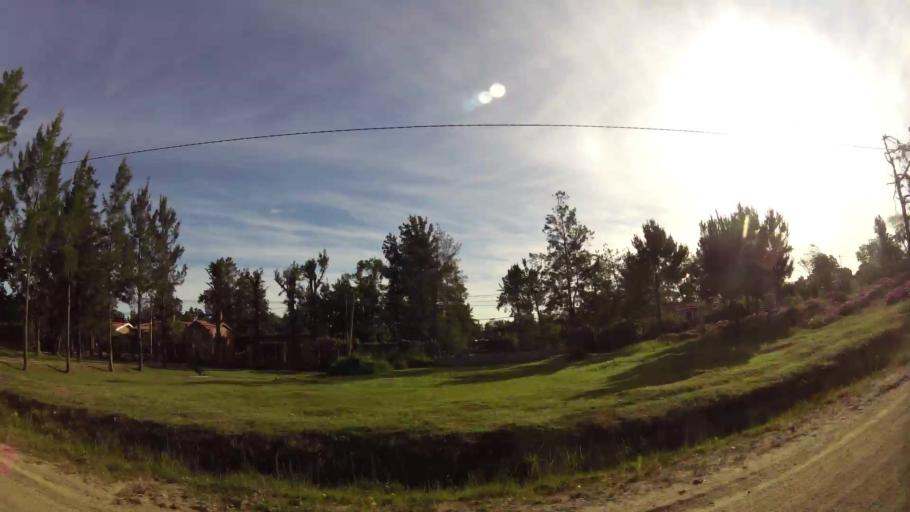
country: UY
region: Canelones
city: Empalme Olmos
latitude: -34.7888
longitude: -55.8583
